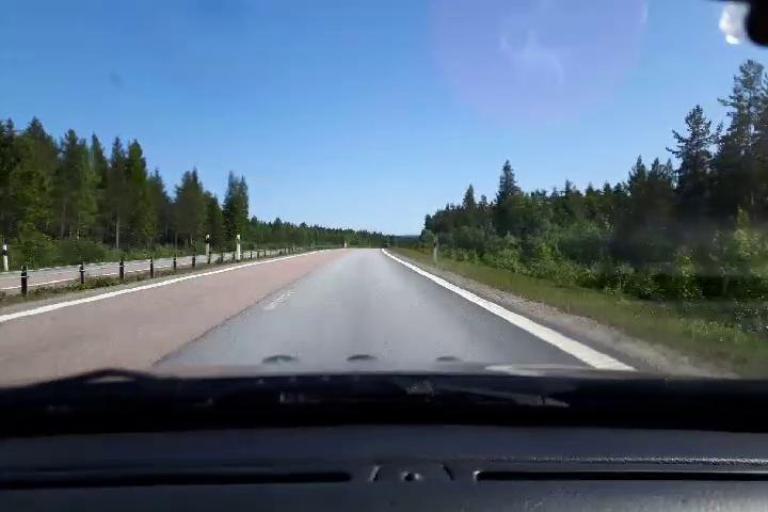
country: SE
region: Gaevleborg
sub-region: Soderhamns Kommun
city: Soderhamn
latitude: 61.3701
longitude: 17.0059
